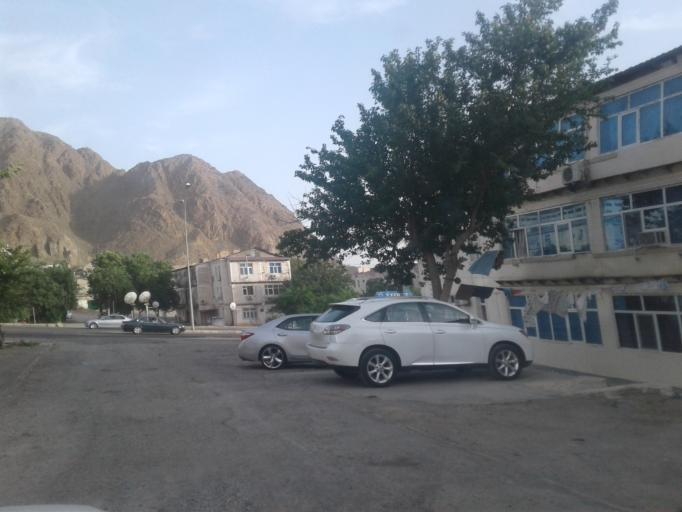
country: TM
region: Balkan
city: Turkmenbasy
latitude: 40.0020
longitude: 52.9767
